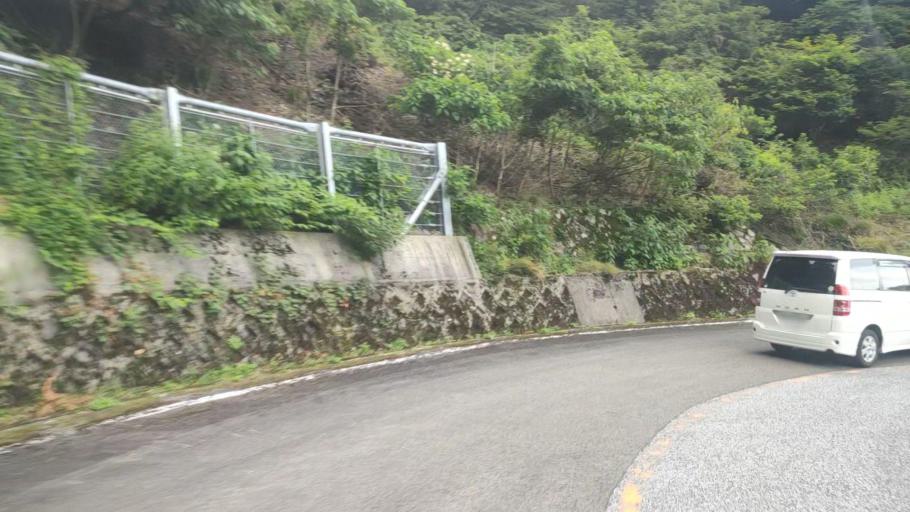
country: JP
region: Gifu
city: Tarui
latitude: 35.3962
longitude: 136.4341
